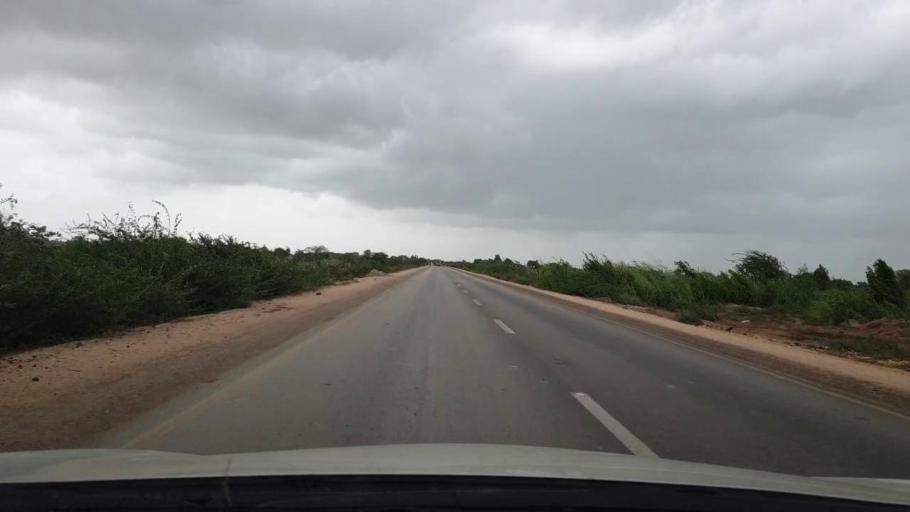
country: PK
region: Sindh
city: Mirpur Batoro
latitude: 24.6428
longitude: 68.4556
